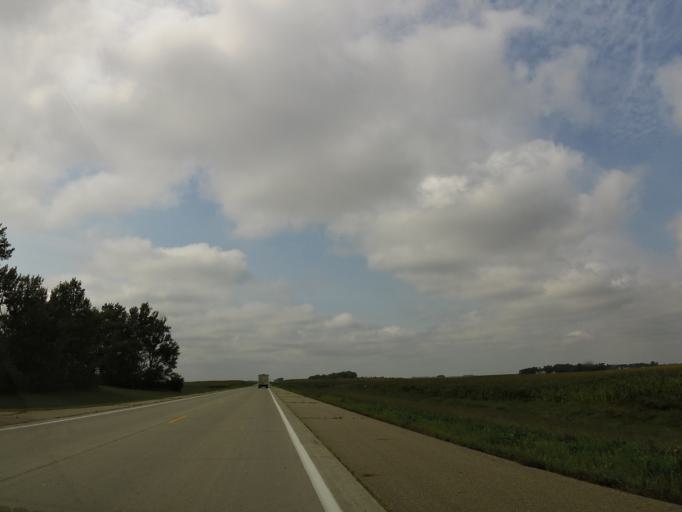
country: US
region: Minnesota
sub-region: Chippewa County
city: Montevideo
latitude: 44.9357
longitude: -95.8449
